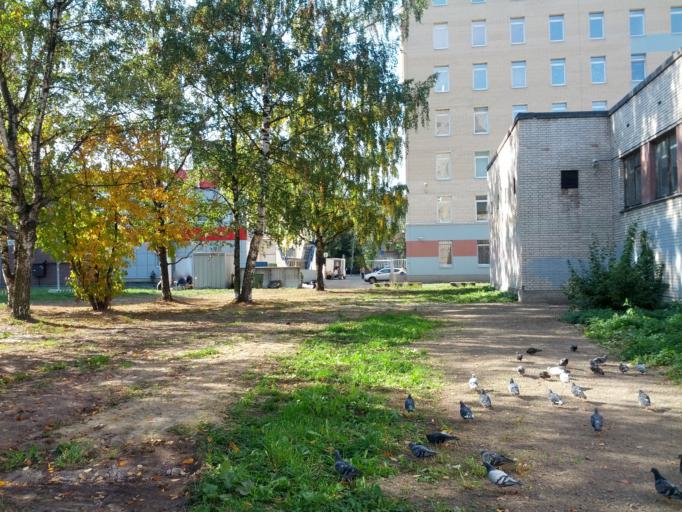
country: RU
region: St.-Petersburg
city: Kupchino
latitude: 59.8347
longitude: 30.3529
